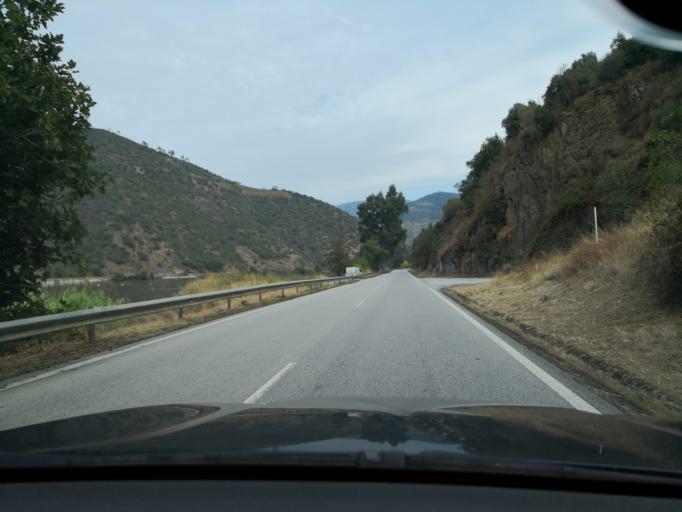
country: PT
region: Viseu
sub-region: Armamar
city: Armamar
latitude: 41.1588
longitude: -7.6693
